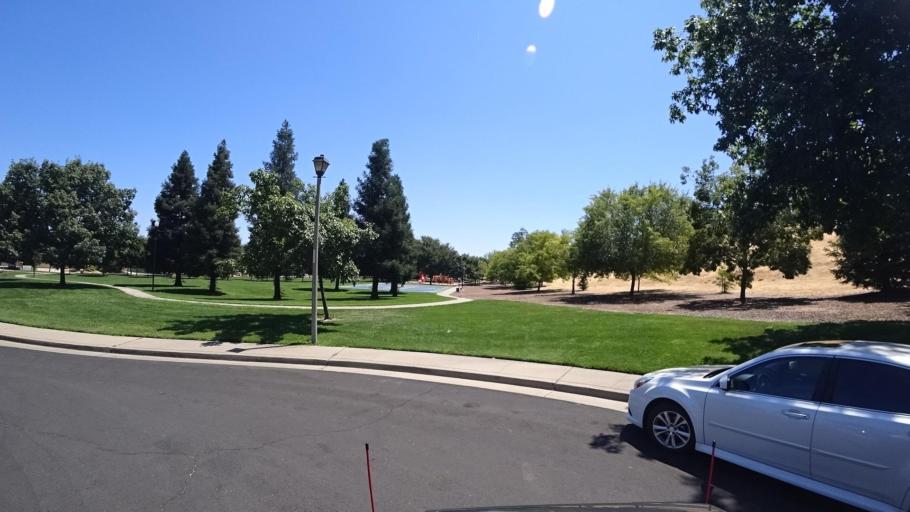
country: US
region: California
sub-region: Placer County
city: Rocklin
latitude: 38.8188
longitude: -121.2701
